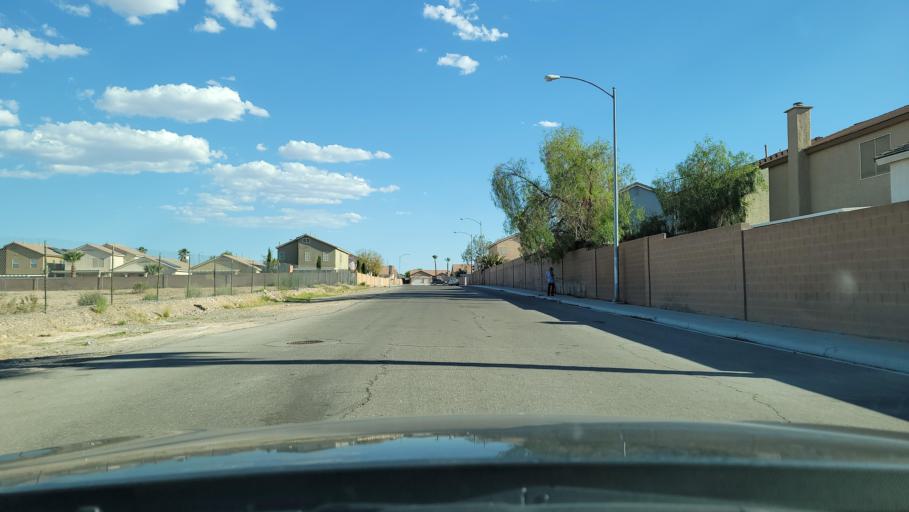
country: US
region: Nevada
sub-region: Clark County
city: Spring Valley
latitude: 36.0832
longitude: -115.2541
